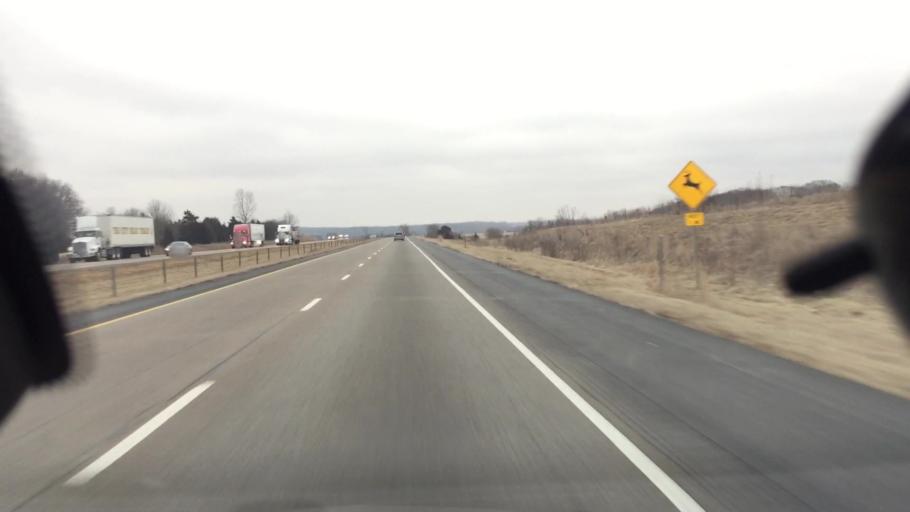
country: US
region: Iowa
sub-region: Muscatine County
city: West Liberty
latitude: 41.6483
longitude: -91.1722
